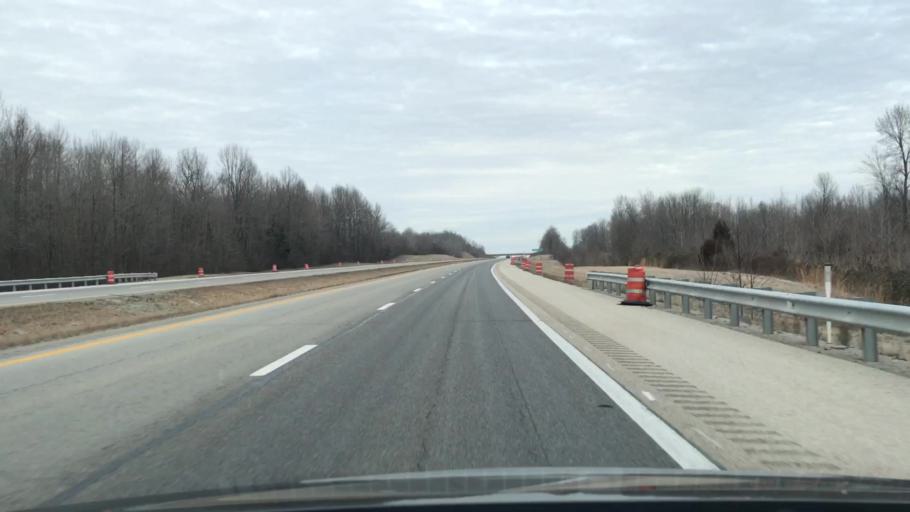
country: US
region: Kentucky
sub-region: Daviess County
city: Masonville
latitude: 37.6084
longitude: -86.9790
